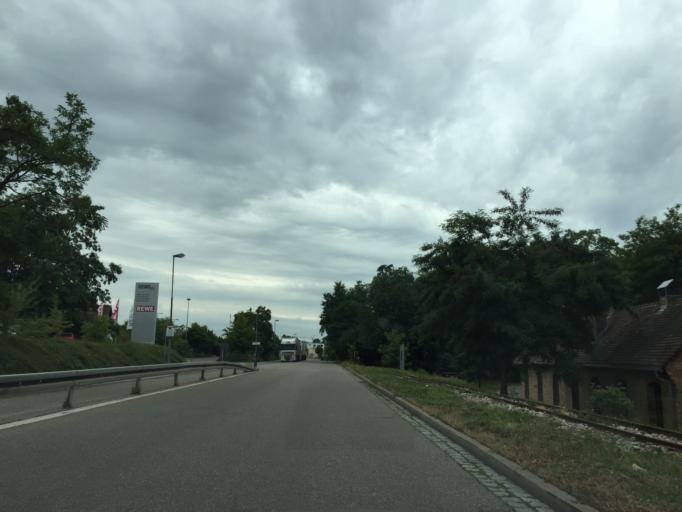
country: DE
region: Baden-Wuerttemberg
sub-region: Karlsruhe Region
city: Walldorf
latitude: 49.2983
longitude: 8.6695
